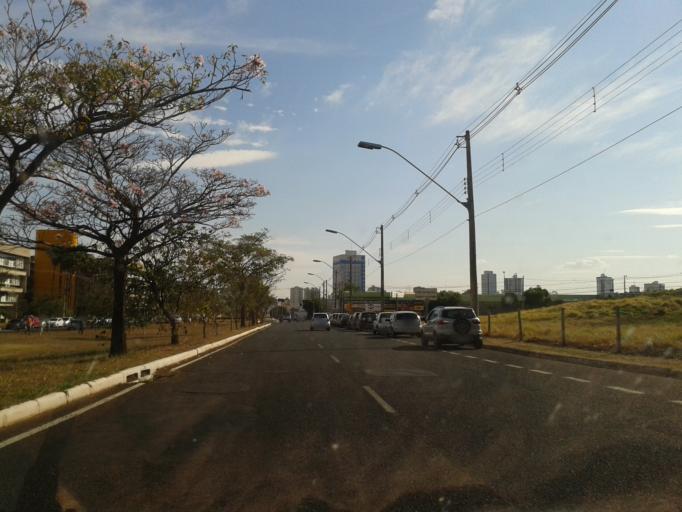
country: BR
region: Minas Gerais
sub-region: Uberlandia
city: Uberlandia
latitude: -18.9108
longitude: -48.2555
